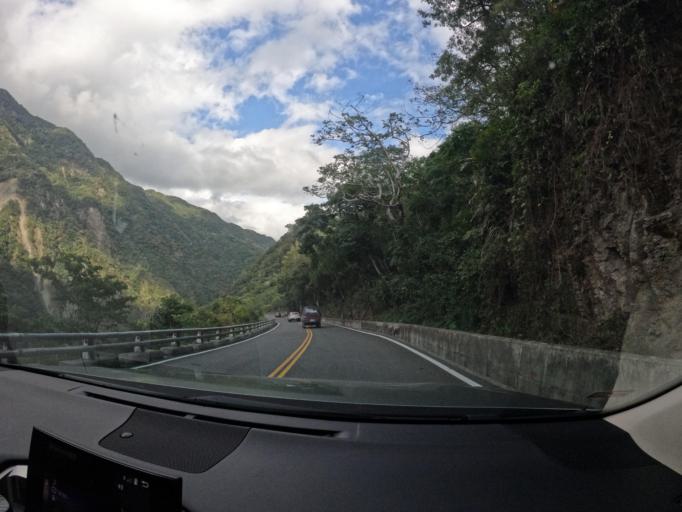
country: TW
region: Taiwan
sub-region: Taitung
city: Taitung
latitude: 23.1507
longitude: 121.0745
